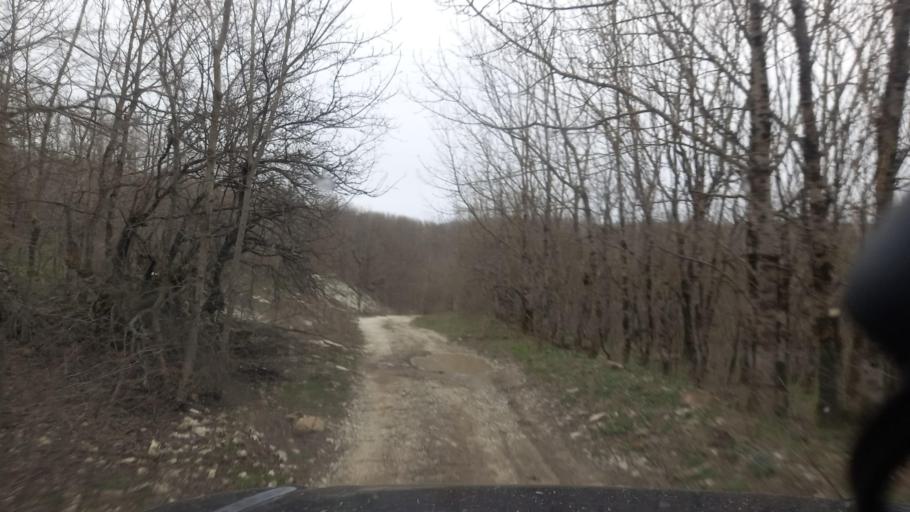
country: RU
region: Krasnodarskiy
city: Divnomorskoye
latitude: 44.6020
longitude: 38.2783
